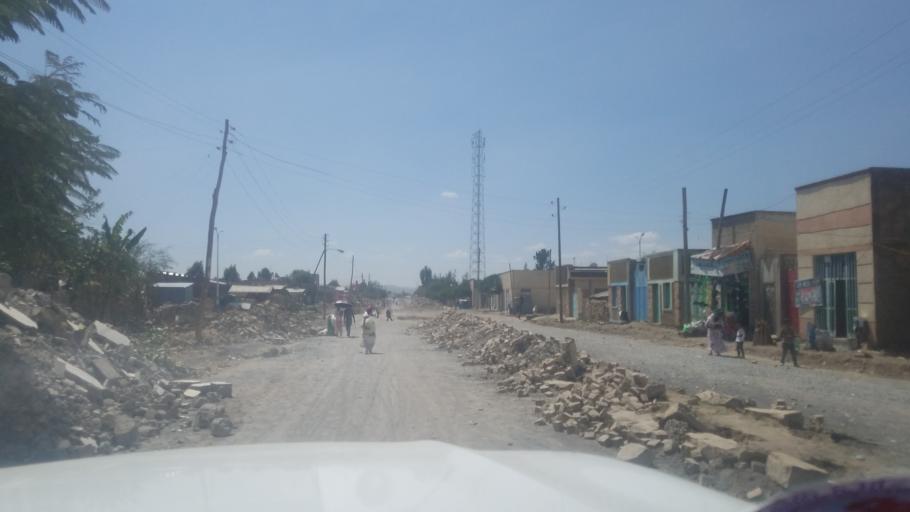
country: ET
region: Tigray
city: Mekele
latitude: 13.7901
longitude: 39.5984
